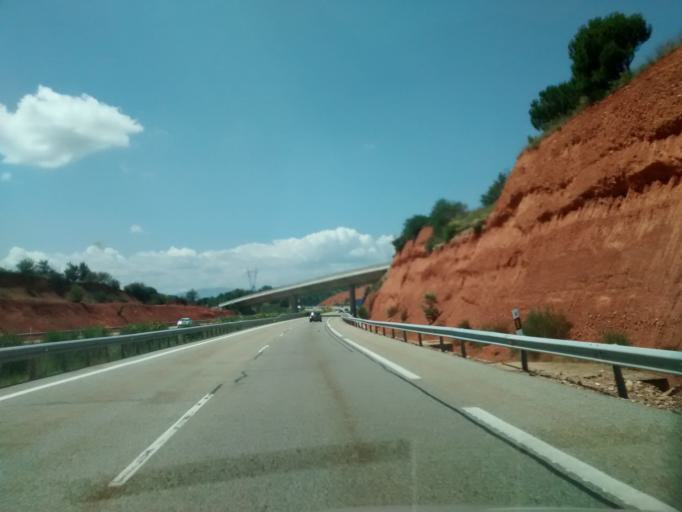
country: ES
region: Castille and Leon
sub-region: Provincia de Leon
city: Brazuelo
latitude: 42.5010
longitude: -6.1217
